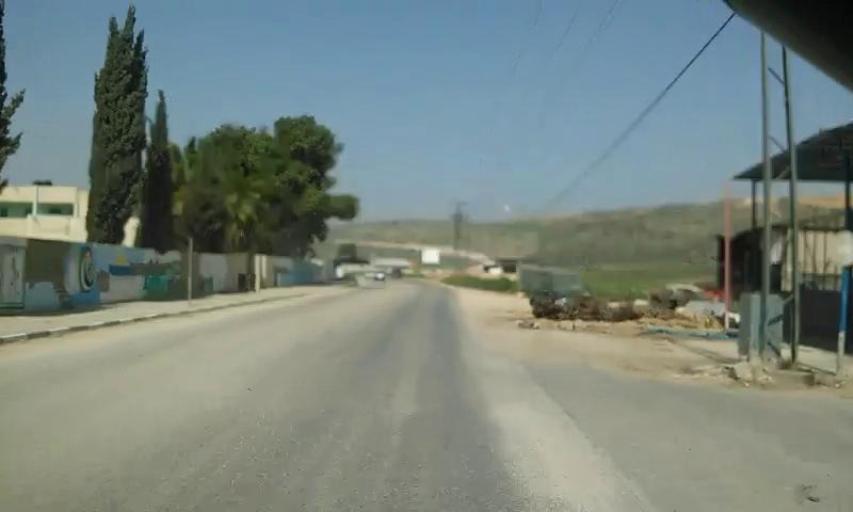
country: PS
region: West Bank
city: Az Zababidah
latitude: 32.3941
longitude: 35.3207
